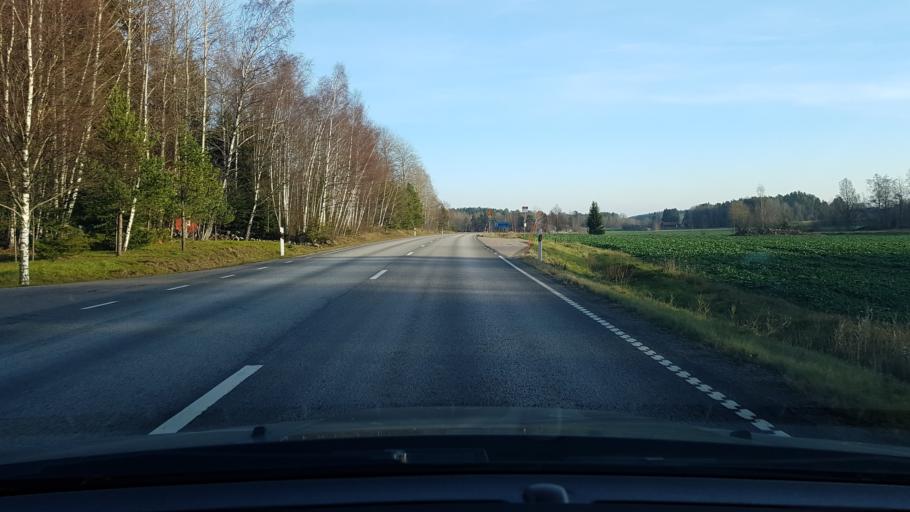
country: SE
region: Stockholm
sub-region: Vallentuna Kommun
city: Vallentuna
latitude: 59.7465
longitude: 18.0917
